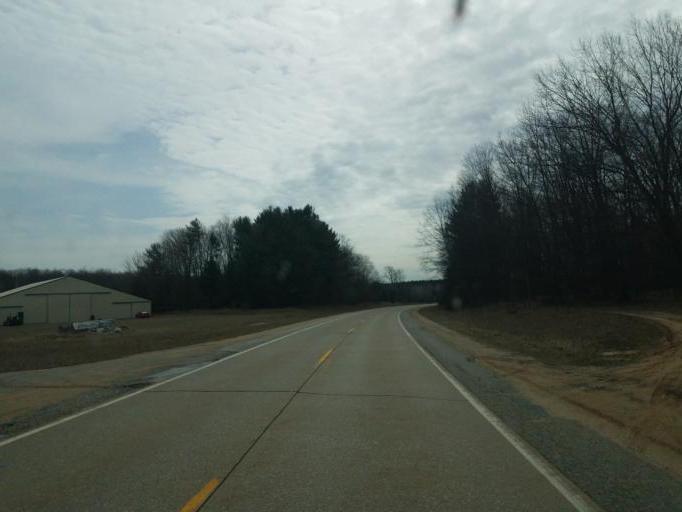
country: US
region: Michigan
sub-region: Oceana County
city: Hart
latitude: 43.7999
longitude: -86.3625
